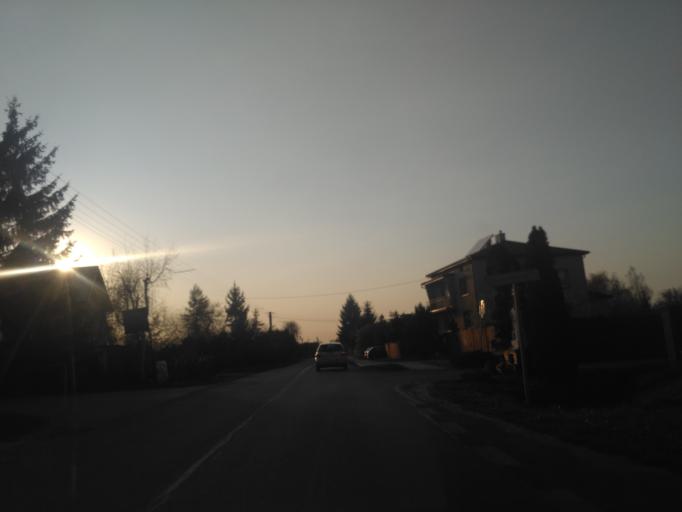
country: PL
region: Lublin Voivodeship
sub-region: Powiat chelmski
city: Pokrowka
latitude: 51.1002
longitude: 23.4803
